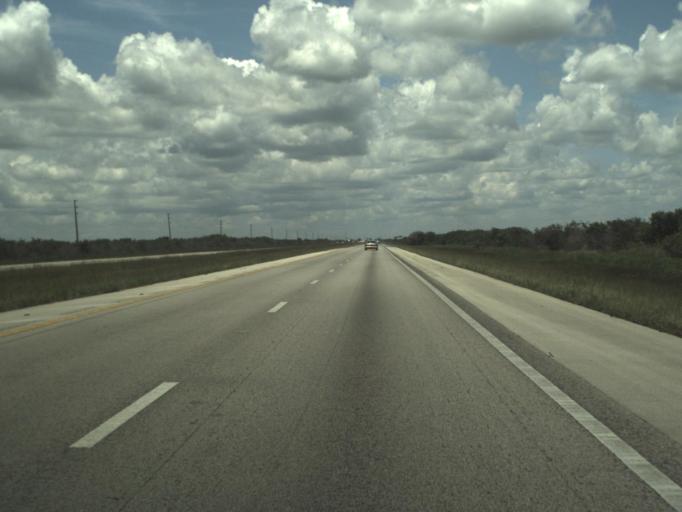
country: US
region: Florida
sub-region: Broward County
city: Weston
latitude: 26.1623
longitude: -80.8005
